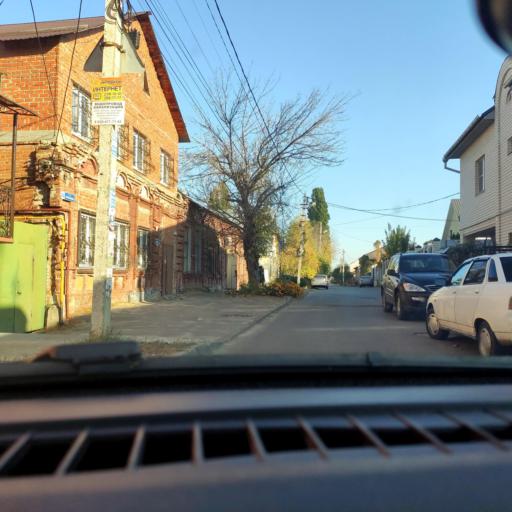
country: RU
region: Voronezj
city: Voronezh
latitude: 51.6767
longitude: 39.2191
